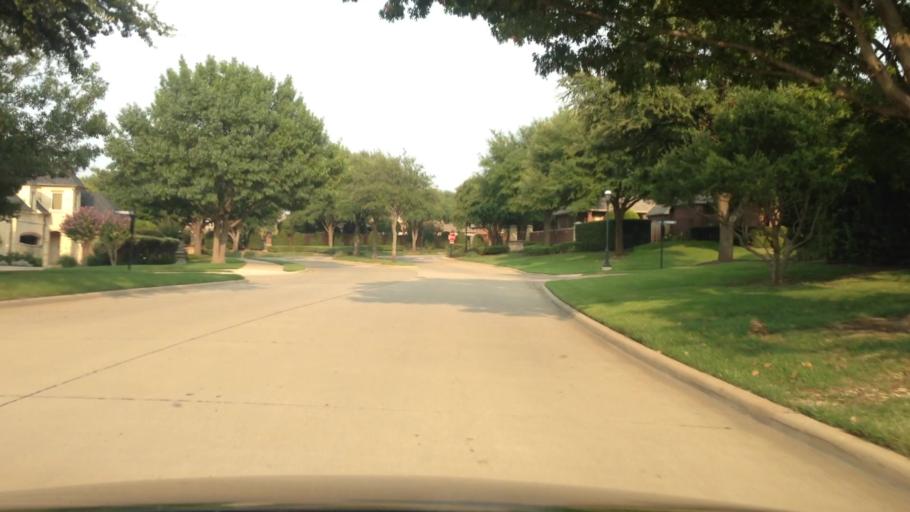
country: US
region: Texas
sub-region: Collin County
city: Frisco
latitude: 33.1286
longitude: -96.8321
